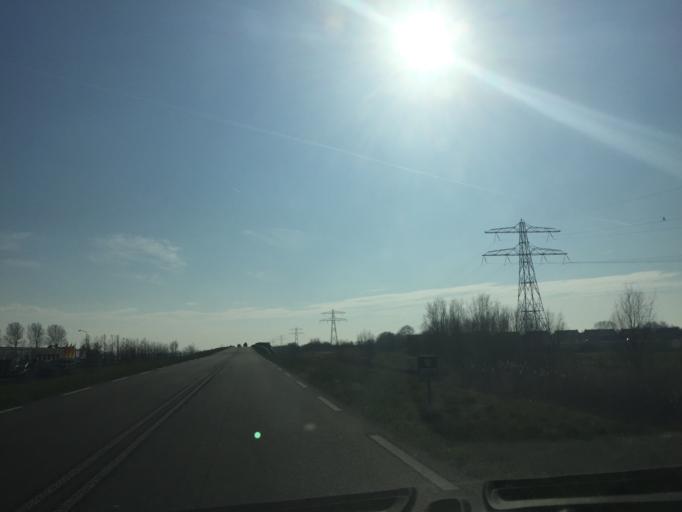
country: NL
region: South Holland
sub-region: Gemeente Hillegom
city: Hillegom
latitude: 52.2845
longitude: 4.6050
